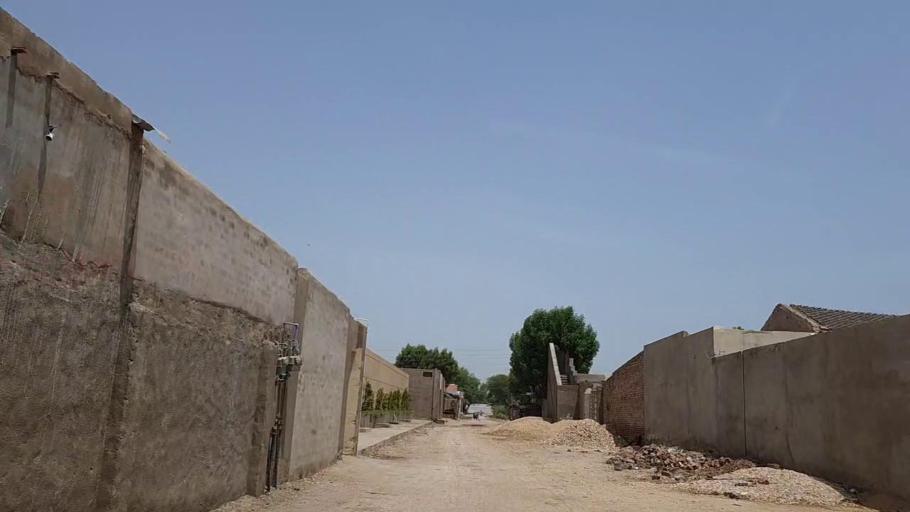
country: PK
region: Sindh
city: Tharu Shah
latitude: 26.9512
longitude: 68.0258
